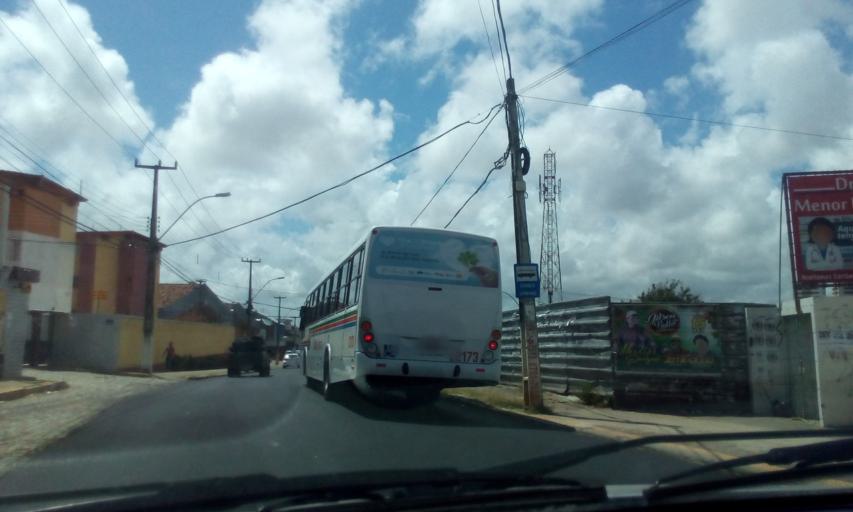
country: BR
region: Rio Grande do Norte
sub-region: Natal
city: Natal
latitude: -5.8549
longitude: -35.2058
